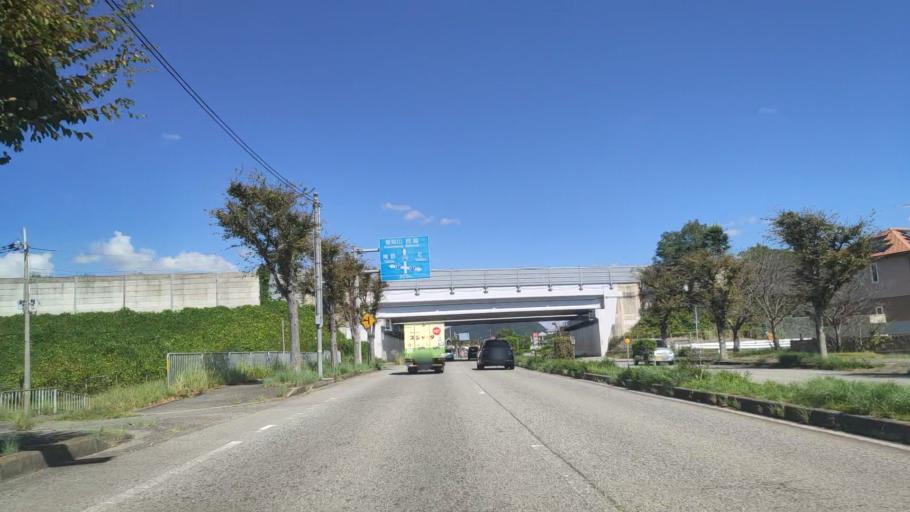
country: JP
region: Hyogo
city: Yashiro
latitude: 34.9291
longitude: 134.9594
